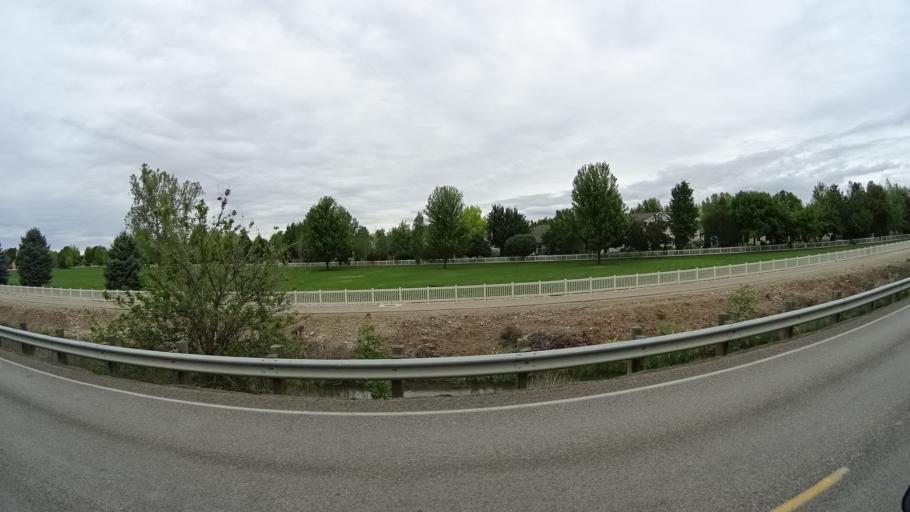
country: US
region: Idaho
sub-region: Ada County
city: Meridian
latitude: 43.6338
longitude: -116.4215
